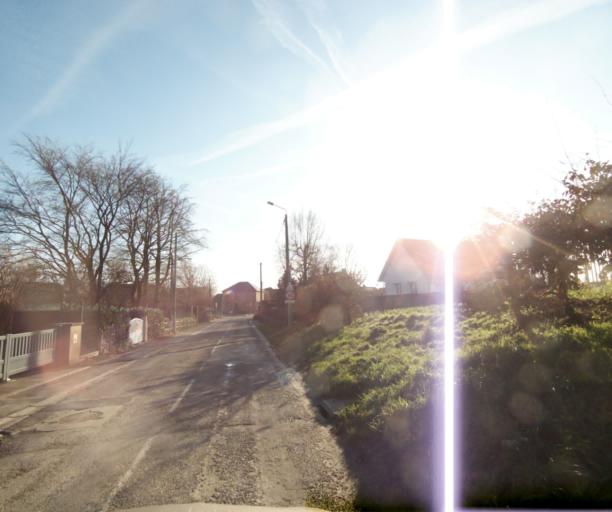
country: FR
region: Nord-Pas-de-Calais
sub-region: Departement du Nord
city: Preseau
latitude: 50.3163
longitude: 3.5747
